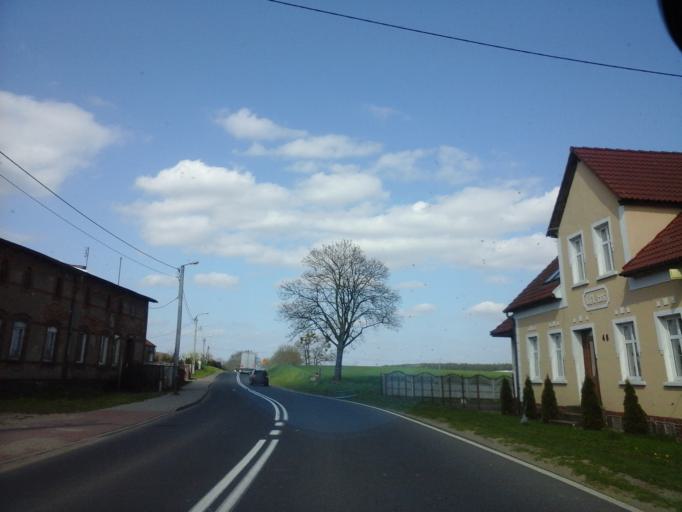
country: PL
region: West Pomeranian Voivodeship
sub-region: Powiat stargardzki
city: Suchan
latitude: 53.2304
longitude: 15.2986
